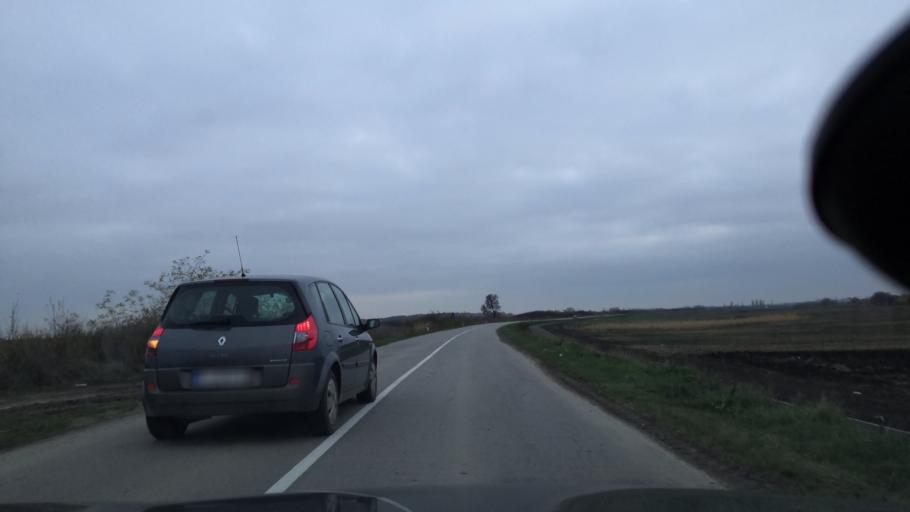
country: RS
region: Autonomna Pokrajina Vojvodina
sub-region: Severnobanatski Okrug
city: Novi Knezevac
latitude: 46.0951
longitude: 20.1101
